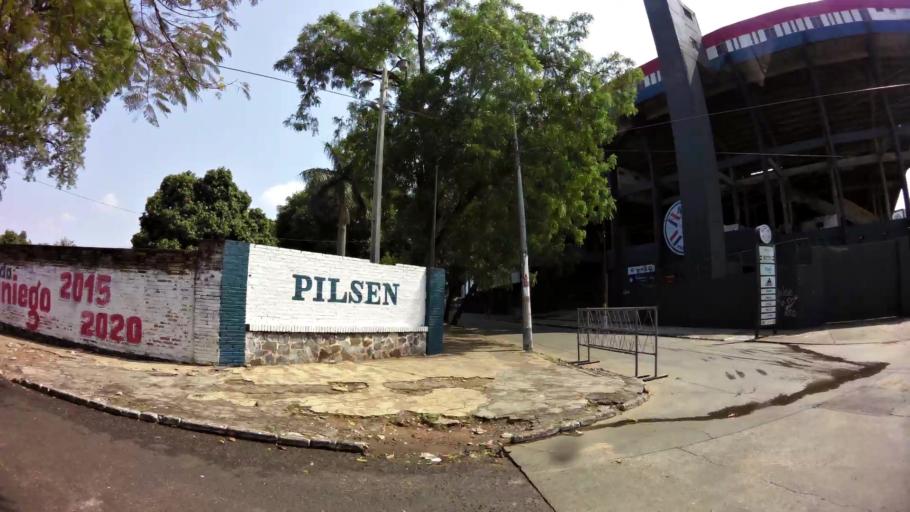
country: PY
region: Asuncion
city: Asuncion
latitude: -25.2931
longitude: -57.6583
